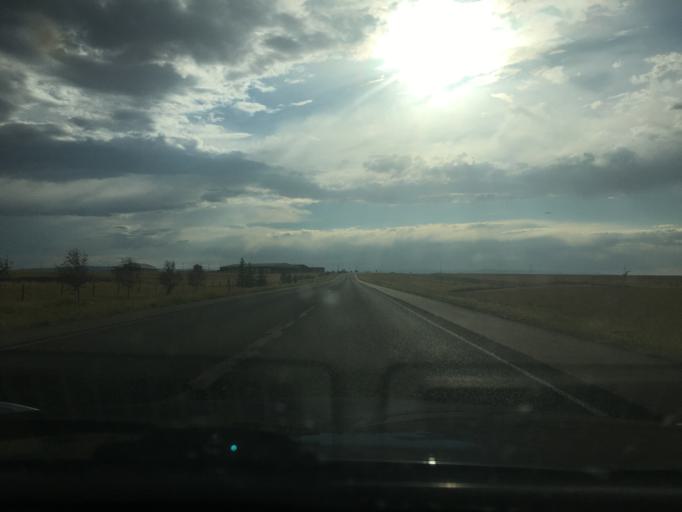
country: US
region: Wyoming
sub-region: Albany County
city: Laramie
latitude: 41.3199
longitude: -105.6463
